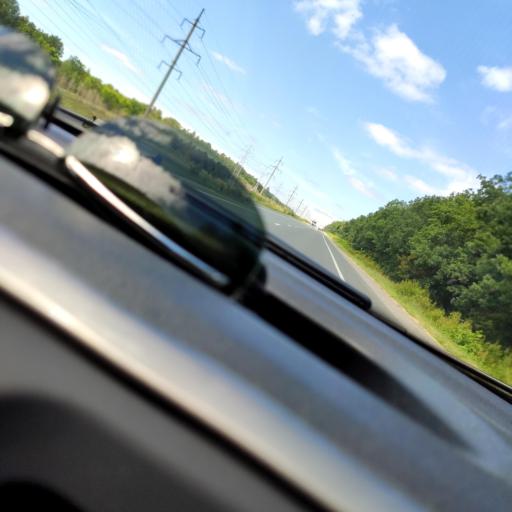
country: RU
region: Samara
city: Bogatyr'
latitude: 53.4965
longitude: 49.9613
